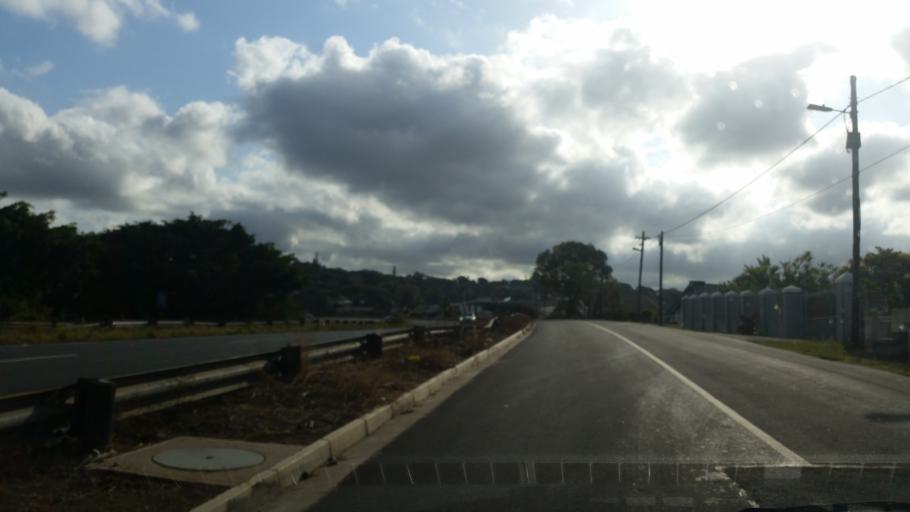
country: ZA
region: KwaZulu-Natal
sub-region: eThekwini Metropolitan Municipality
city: Berea
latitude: -29.8300
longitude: 30.9462
